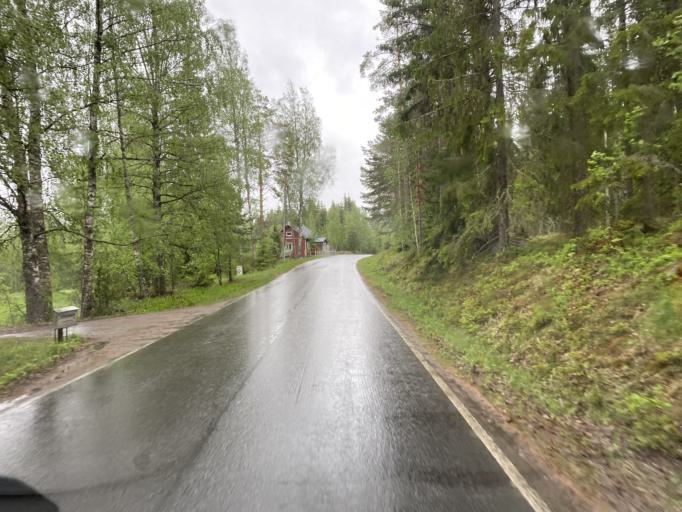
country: FI
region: Haeme
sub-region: Forssa
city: Humppila
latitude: 61.0717
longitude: 23.3147
